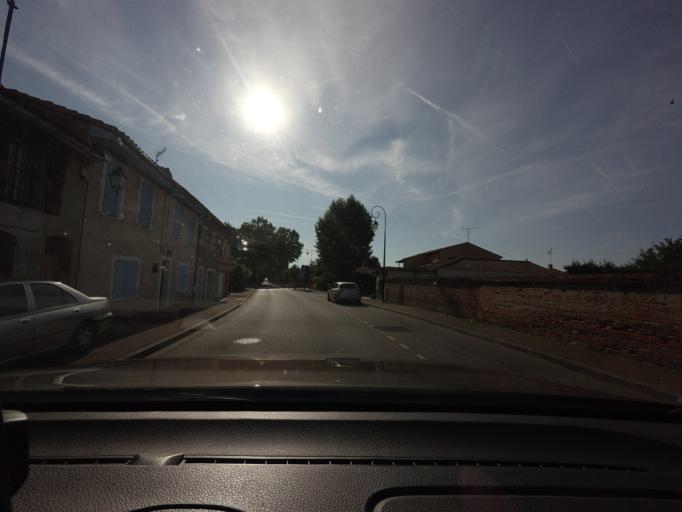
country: FR
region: Midi-Pyrenees
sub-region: Departement de la Haute-Garonne
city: Pibrac
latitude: 43.6166
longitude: 1.2877
